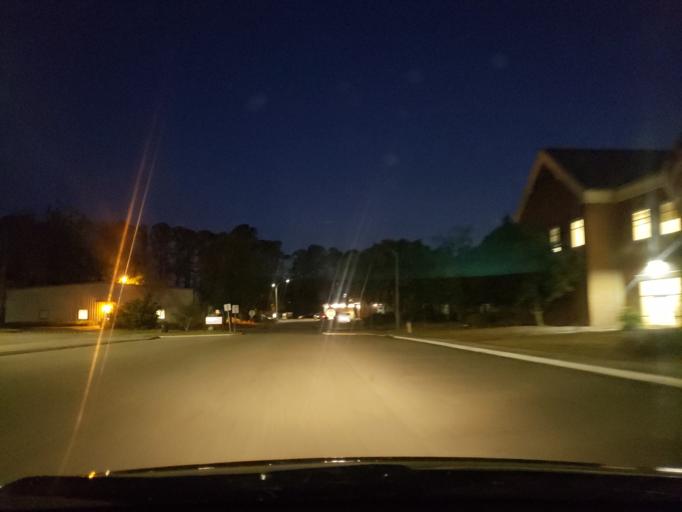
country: US
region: Georgia
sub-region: Chatham County
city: Montgomery
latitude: 31.9797
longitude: -81.1603
